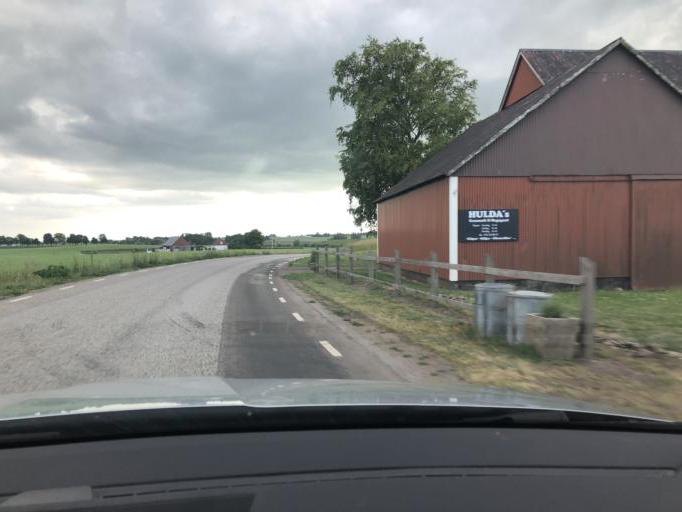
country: SE
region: Skane
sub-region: Simrishamns Kommun
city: Simrishamn
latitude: 55.5091
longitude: 14.2297
